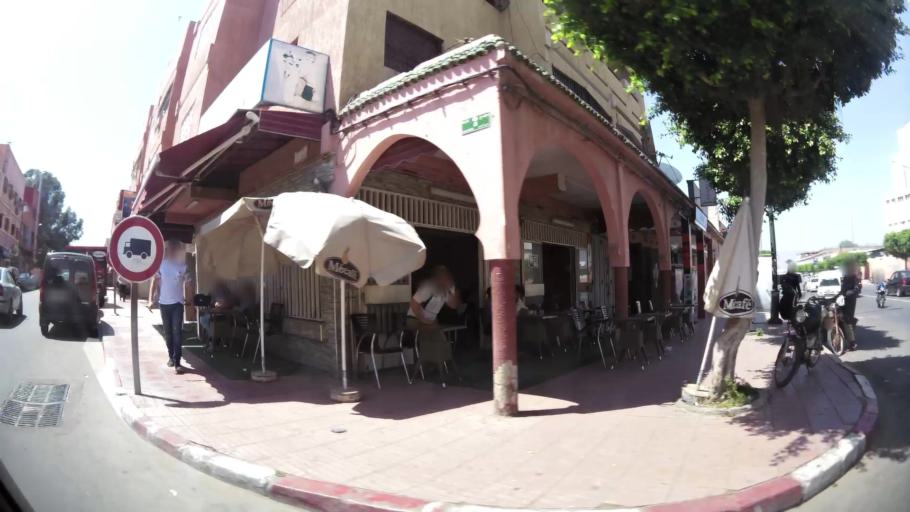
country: MA
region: Souss-Massa-Draa
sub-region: Inezgane-Ait Mellou
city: Inezgane
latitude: 30.3459
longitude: -9.5030
